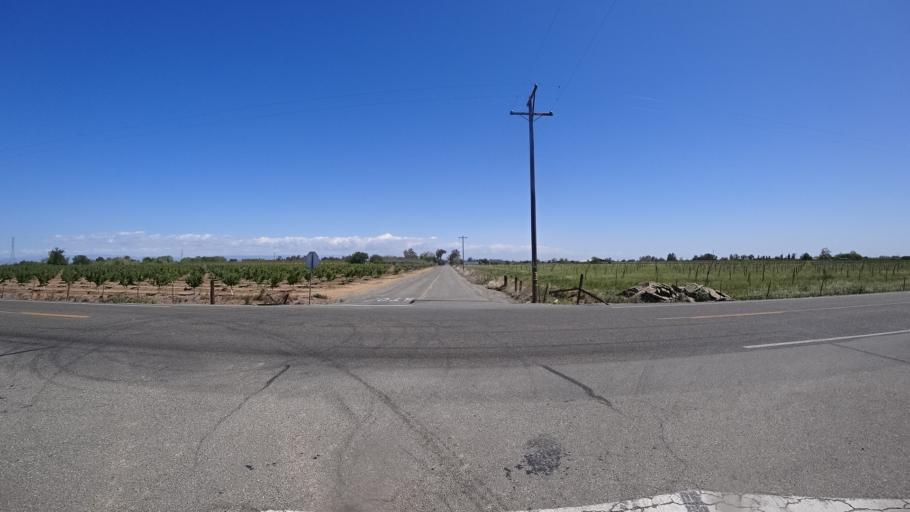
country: US
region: California
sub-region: Glenn County
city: Orland
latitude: 39.7944
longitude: -122.1972
